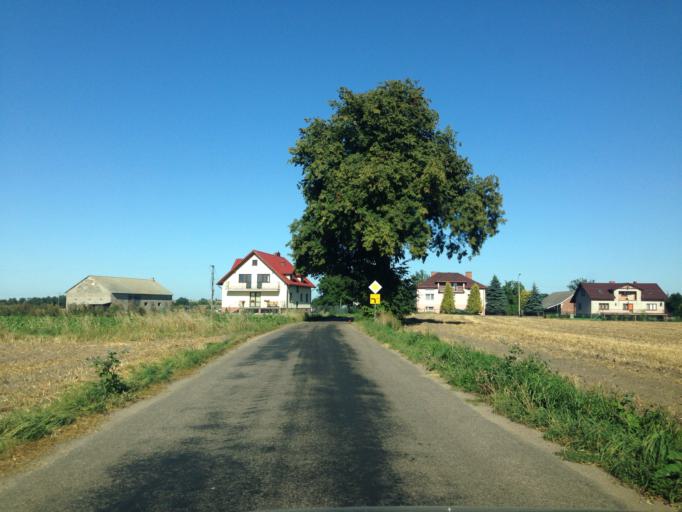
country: PL
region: Kujawsko-Pomorskie
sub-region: Powiat brodnicki
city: Swiedziebnia
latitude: 53.2002
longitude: 19.5452
